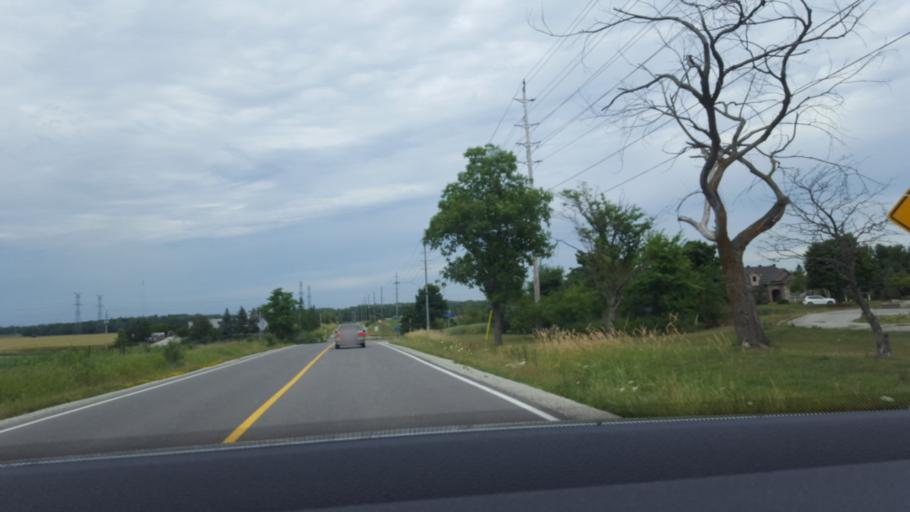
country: CA
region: Ontario
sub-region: Halton
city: Milton
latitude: 43.5576
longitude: -79.9024
